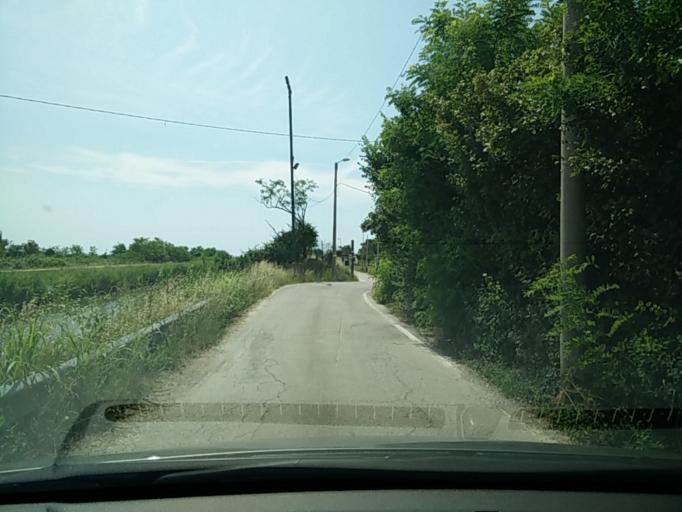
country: IT
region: Veneto
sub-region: Provincia di Venezia
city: Tessera
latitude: 45.5000
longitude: 12.3314
